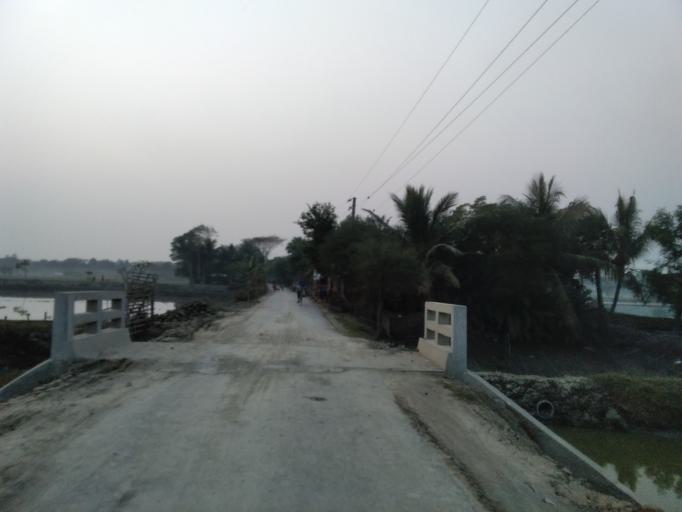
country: BD
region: Khulna
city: Satkhira
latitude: 22.6503
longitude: 89.0027
